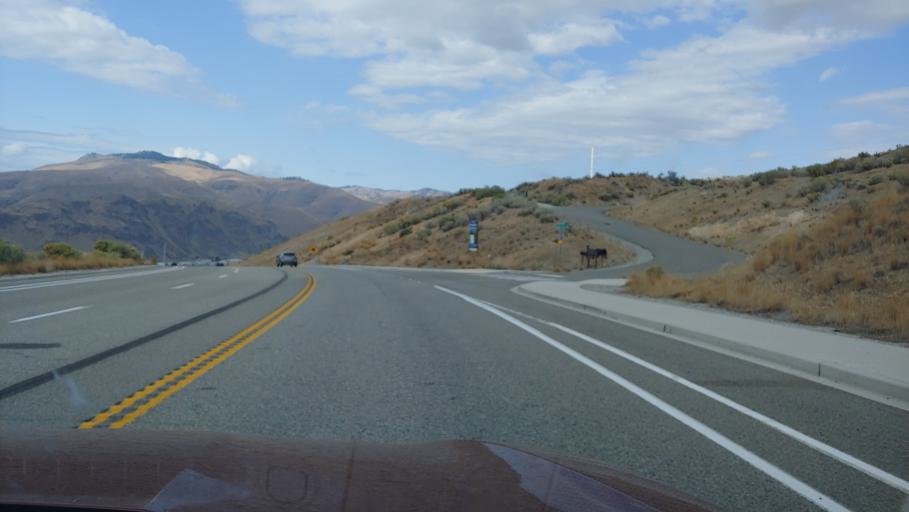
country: US
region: Washington
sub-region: Douglas County
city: East Wenatchee Bench
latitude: 47.4590
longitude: -120.2925
